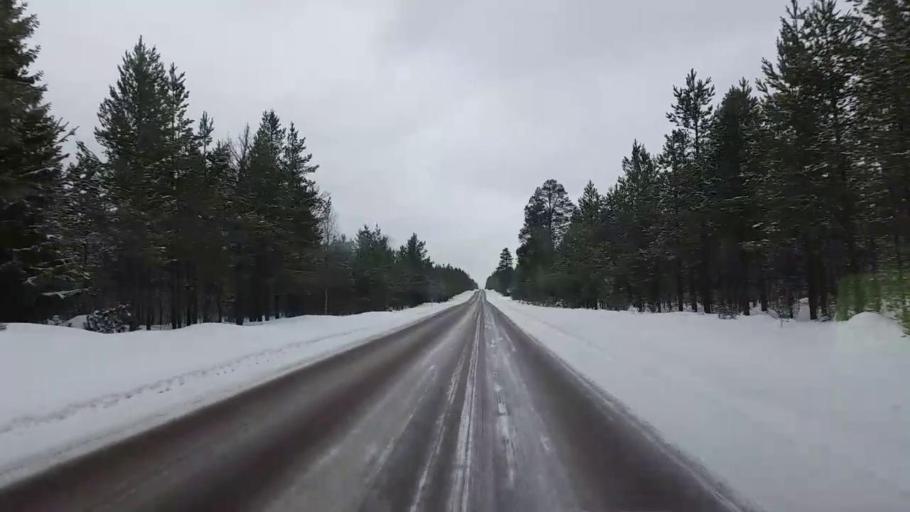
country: SE
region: Jaemtland
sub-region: Bergs Kommun
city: Hoverberg
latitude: 62.4376
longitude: 14.5853
